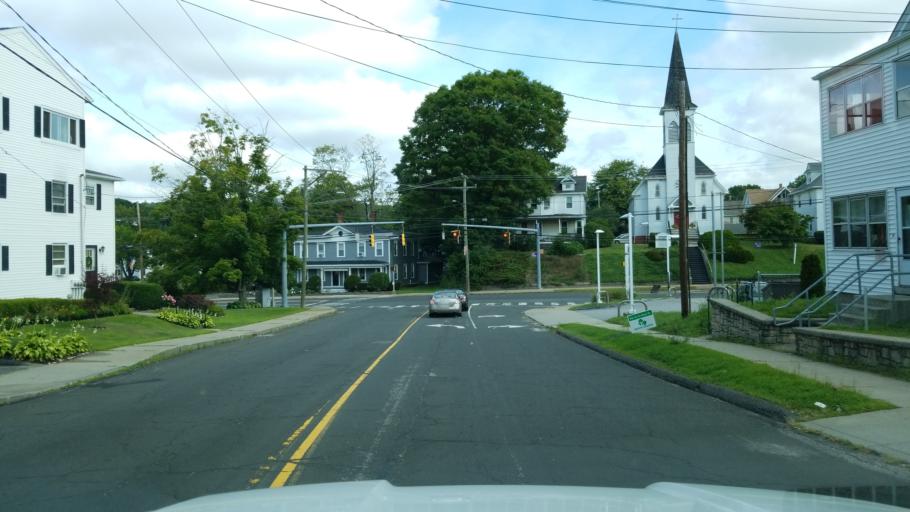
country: US
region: Connecticut
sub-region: Litchfield County
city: Terryville
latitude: 41.6780
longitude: -73.0037
